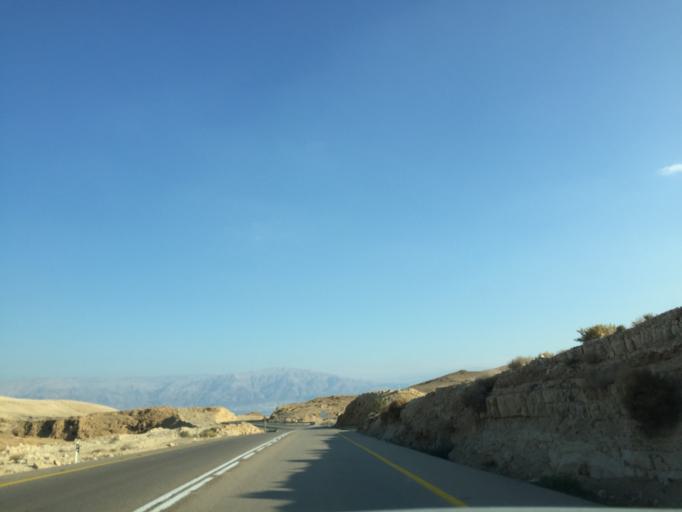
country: IL
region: Southern District
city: `En Boqeq
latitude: 31.1621
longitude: 35.3255
